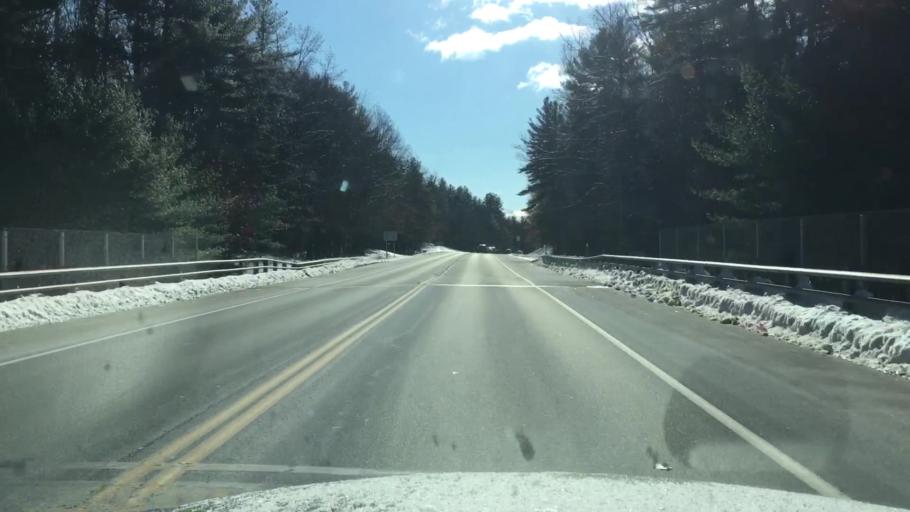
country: US
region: New Hampshire
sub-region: Hillsborough County
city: Milford
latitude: 42.8581
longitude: -71.6115
